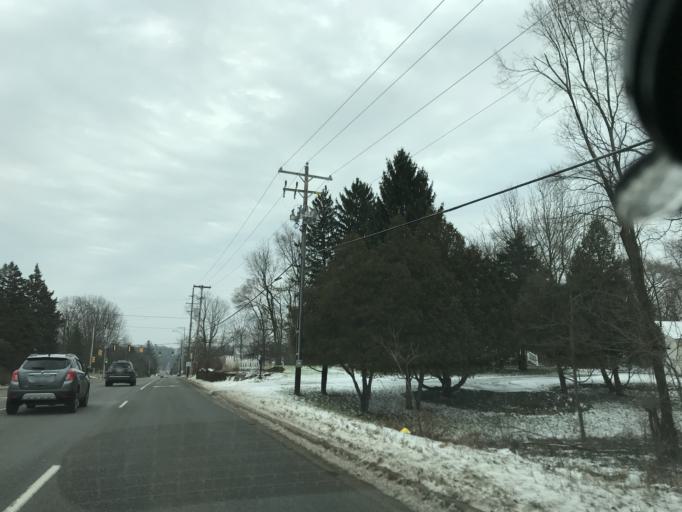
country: US
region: Michigan
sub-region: Kent County
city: Rockford
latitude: 43.1172
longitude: -85.5722
